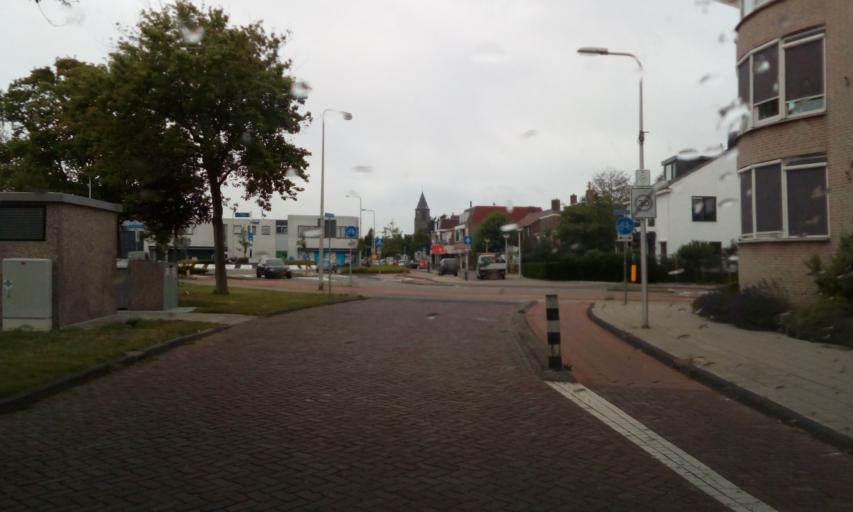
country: NL
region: South Holland
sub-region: Gemeente Westland
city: Honselersdijk
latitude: 52.0093
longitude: 4.2308
